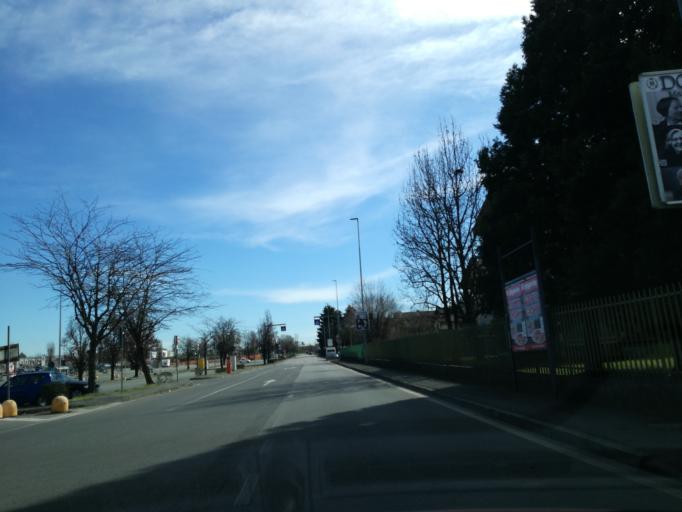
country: IT
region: Lombardy
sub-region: Provincia di Monza e Brianza
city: Villasanta
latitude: 45.6174
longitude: 9.3066
